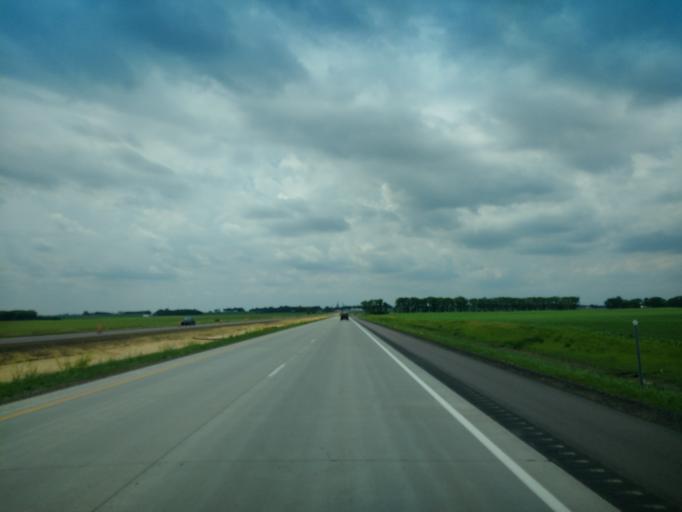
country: US
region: Minnesota
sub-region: Cottonwood County
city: Mountain Lake
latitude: 43.9164
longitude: -95.0086
